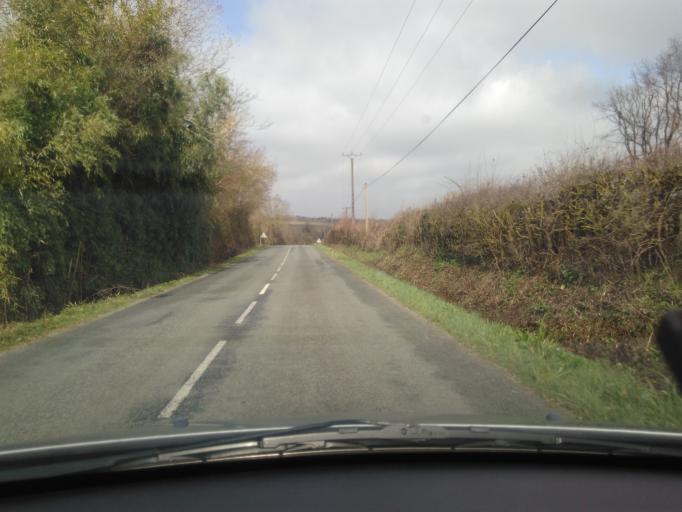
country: FR
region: Pays de la Loire
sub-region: Departement de la Vendee
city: Sainte-Cecile
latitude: 46.6970
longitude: -1.1286
